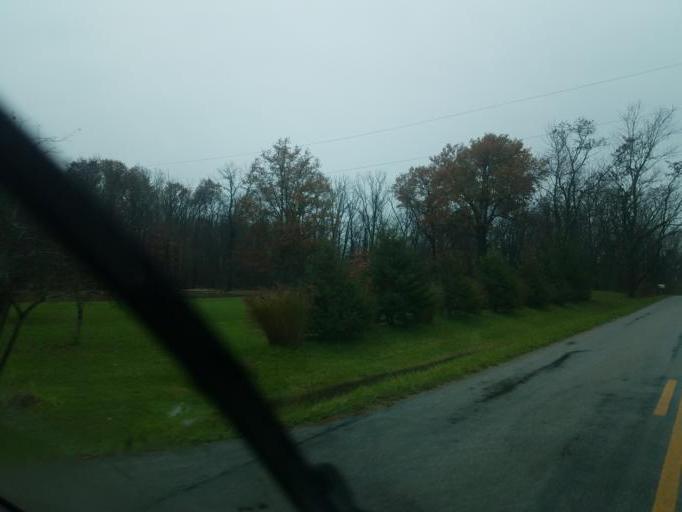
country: US
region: Ohio
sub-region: Delaware County
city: Sunbury
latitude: 40.2961
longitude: -82.7970
